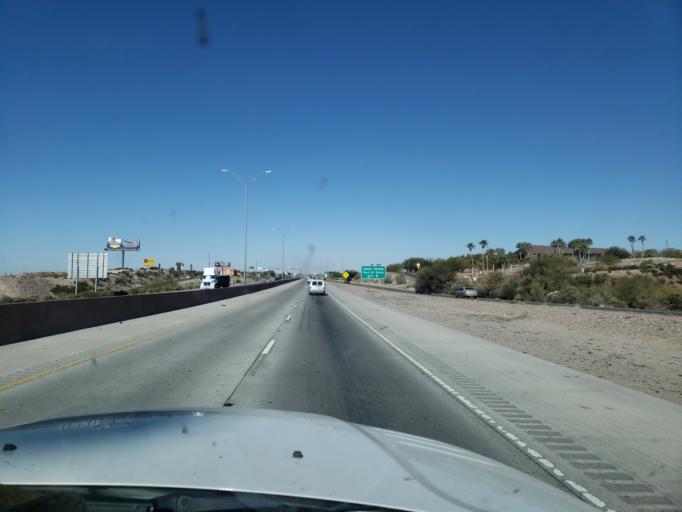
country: US
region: Texas
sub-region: El Paso County
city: Canutillo
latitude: 31.8701
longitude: -106.5787
